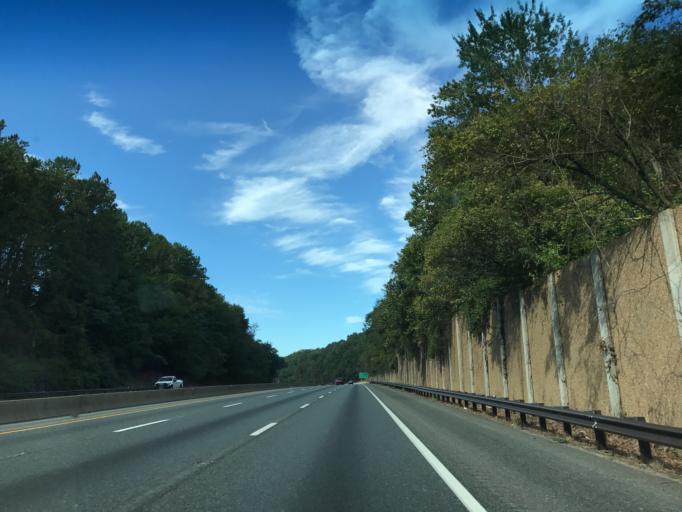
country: US
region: Maryland
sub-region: Anne Arundel County
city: Riva
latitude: 38.9840
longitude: -76.5953
